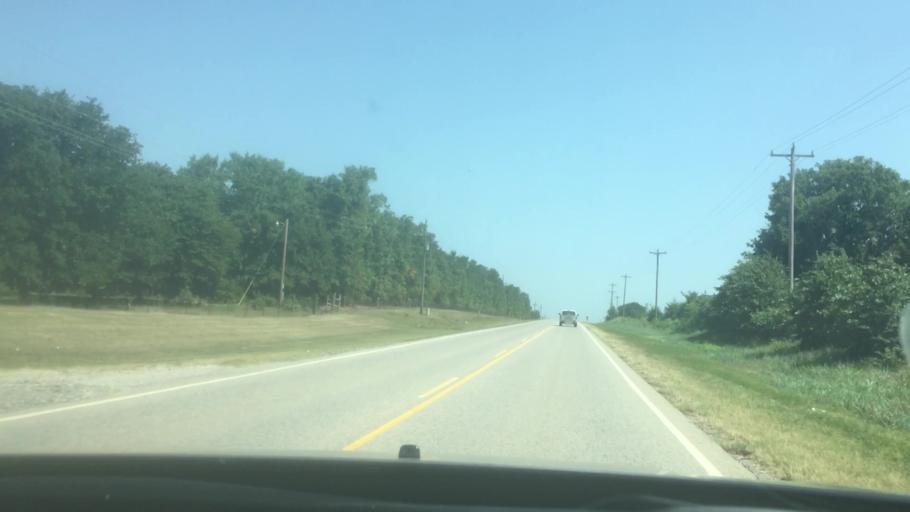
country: US
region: Oklahoma
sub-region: Bryan County
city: Durant
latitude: 34.2236
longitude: -96.4249
